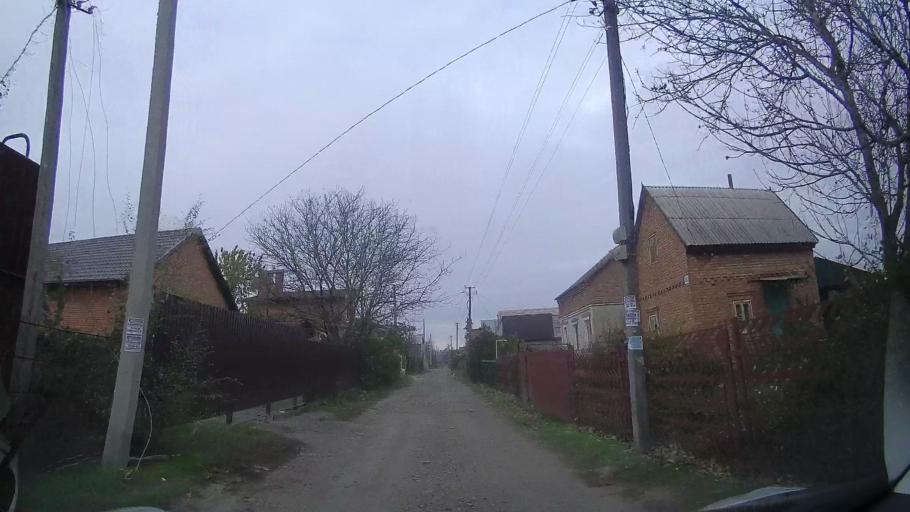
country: RU
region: Rostov
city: Bataysk
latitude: 47.0831
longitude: 39.7570
